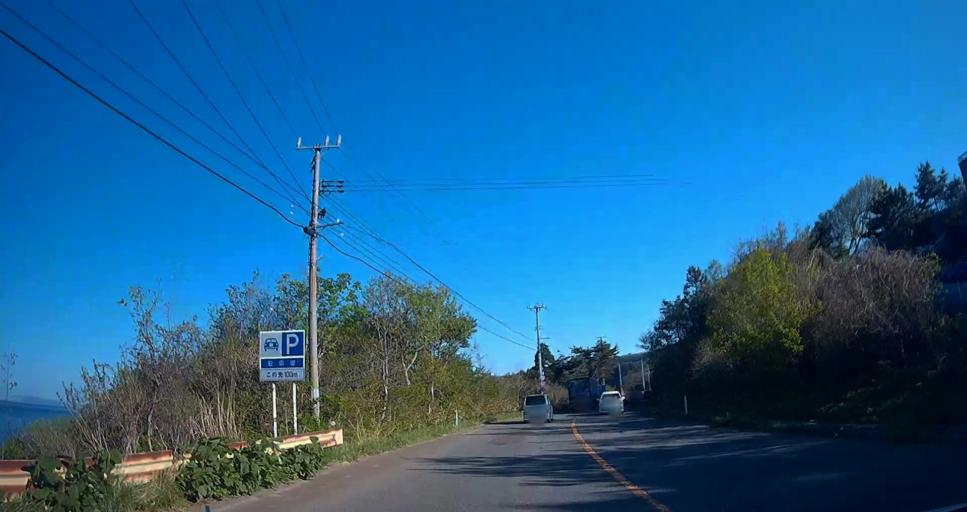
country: JP
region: Aomori
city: Mutsu
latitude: 41.4530
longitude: 141.1191
